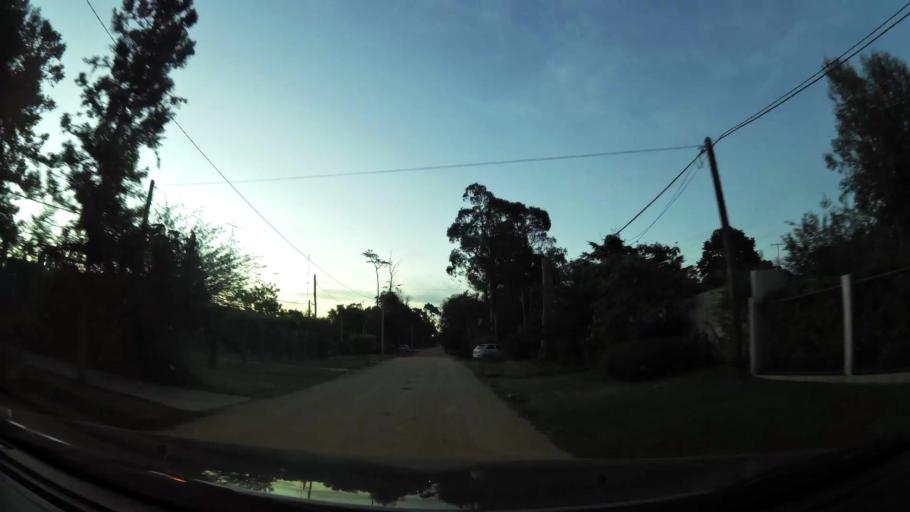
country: UY
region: Canelones
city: Atlantida
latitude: -34.7680
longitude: -55.7553
